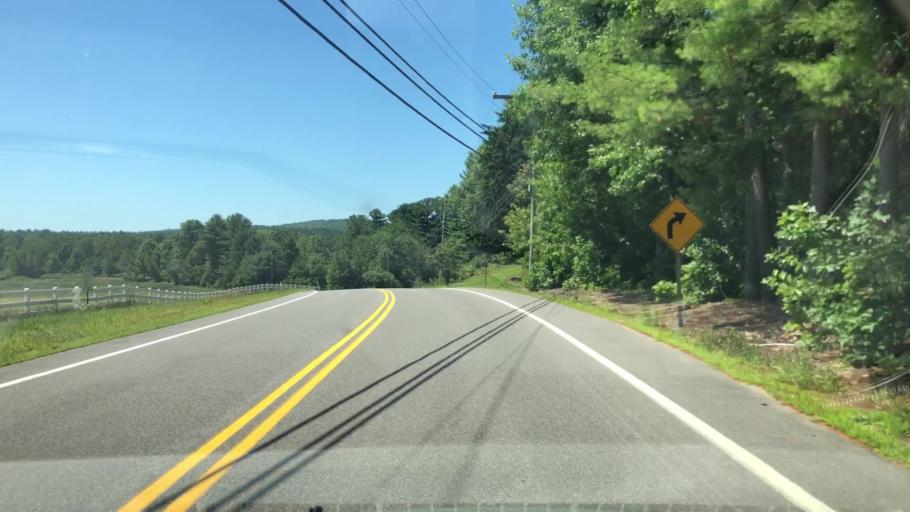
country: US
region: New Hampshire
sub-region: Hillsborough County
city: Milford
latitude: 42.8373
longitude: -71.6081
